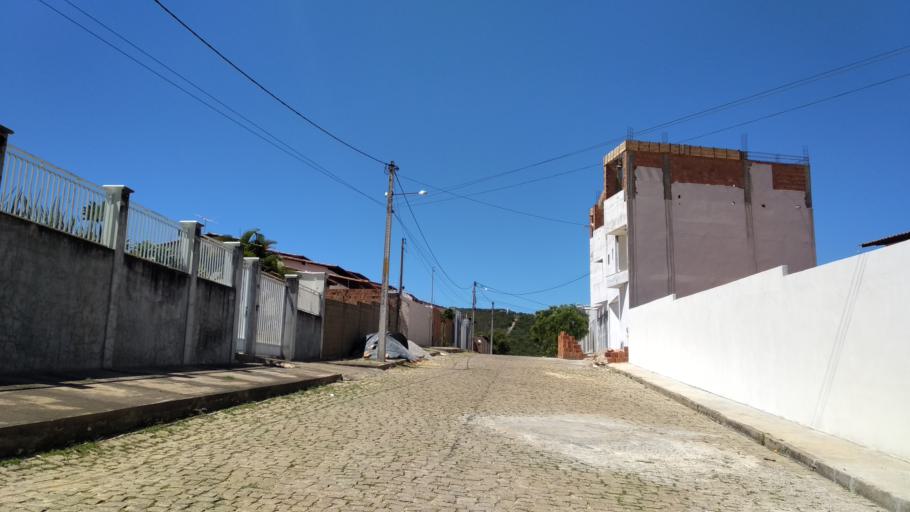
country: BR
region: Bahia
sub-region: Caetite
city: Caetite
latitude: -14.0738
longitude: -42.4806
